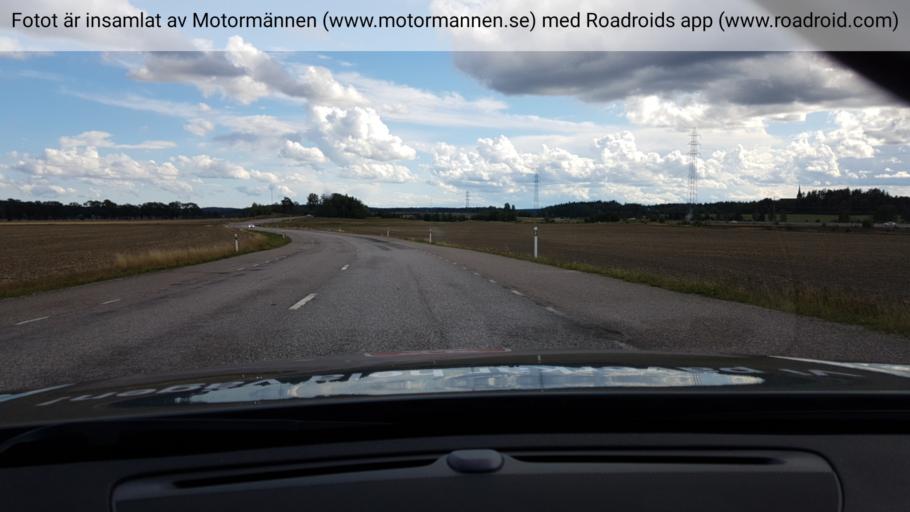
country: SE
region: Soedermanland
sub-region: Strangnas Kommun
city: Akers Styckebruk
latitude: 59.2876
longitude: 17.1086
